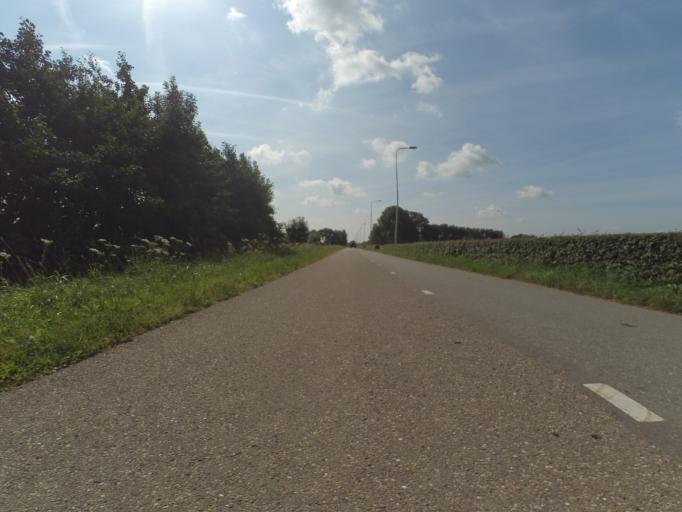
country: NL
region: Utrecht
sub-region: Gemeente Bunnik
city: Bunnik
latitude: 52.0419
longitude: 5.2319
